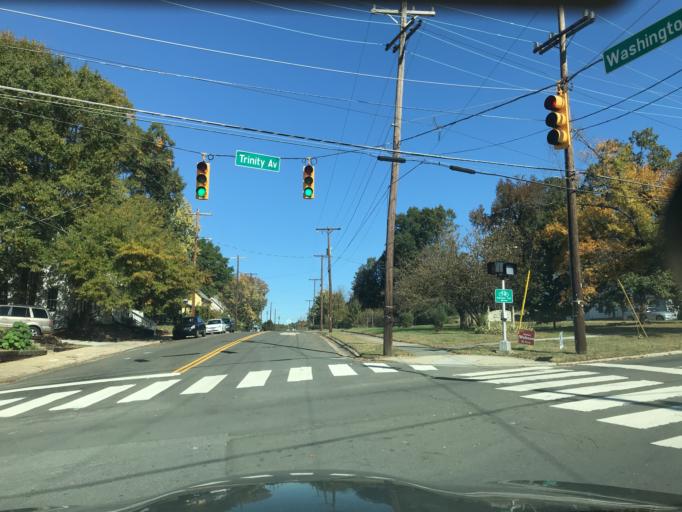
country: US
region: North Carolina
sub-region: Durham County
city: Durham
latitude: 36.0054
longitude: -78.9020
